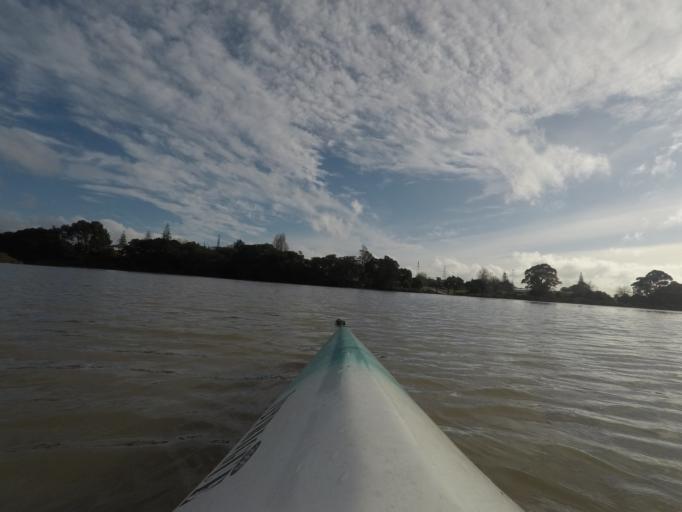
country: NZ
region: Auckland
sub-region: Auckland
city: Rosebank
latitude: -36.8966
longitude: 174.6738
